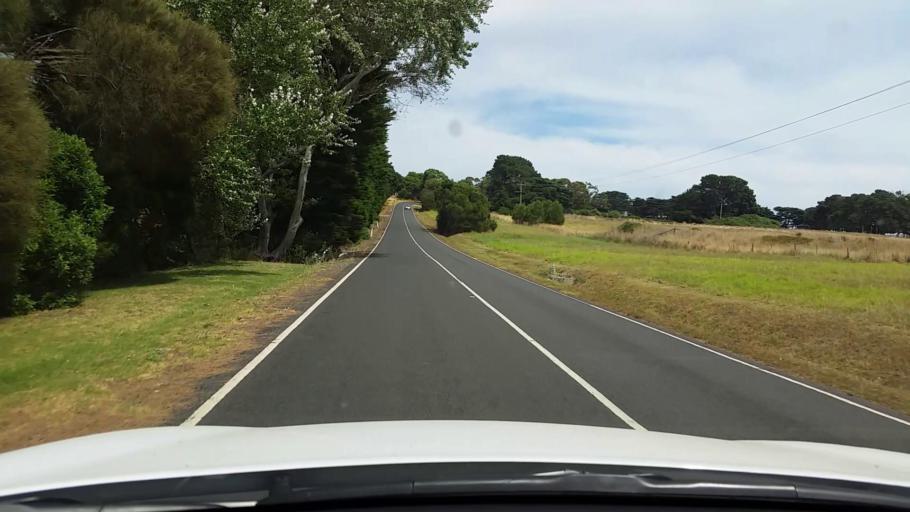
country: AU
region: Victoria
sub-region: Mornington Peninsula
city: McCrae
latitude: -38.4812
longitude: 144.9806
